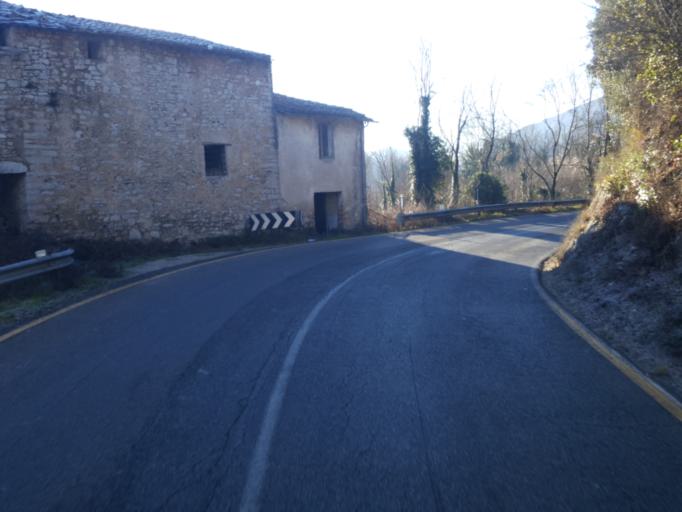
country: IT
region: Umbria
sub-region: Provincia di Terni
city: Arrone
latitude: 42.5344
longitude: 12.7313
